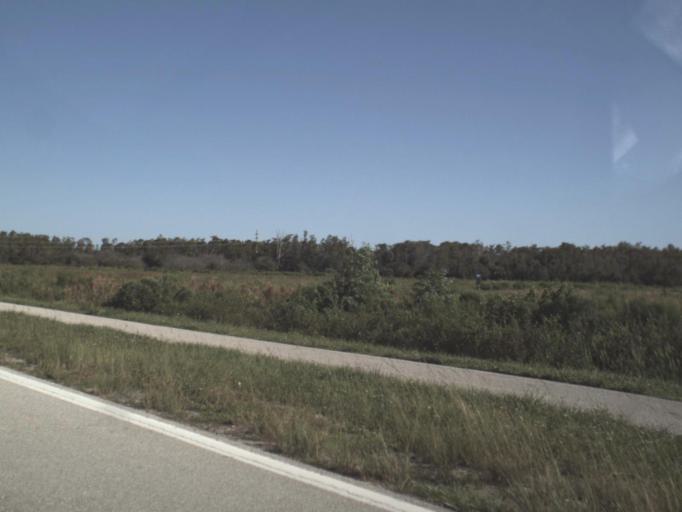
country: US
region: Florida
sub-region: Lee County
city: Villas
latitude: 26.5281
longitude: -81.8514
